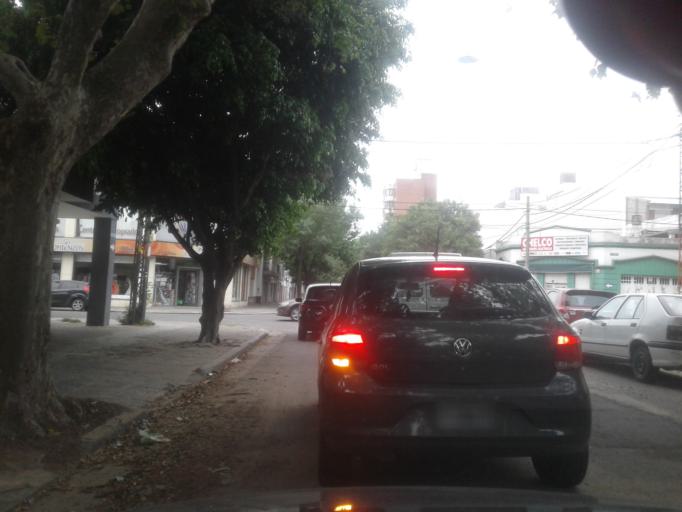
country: AR
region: Santa Fe
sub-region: Departamento de Rosario
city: Rosario
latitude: -32.9464
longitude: -60.6767
